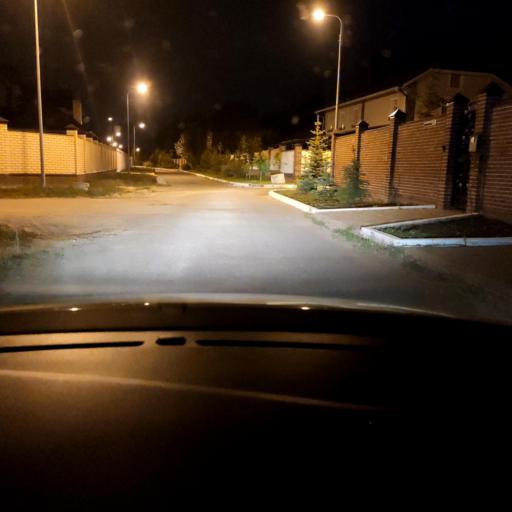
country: RU
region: Tatarstan
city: Osinovo
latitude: 55.8589
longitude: 48.7948
